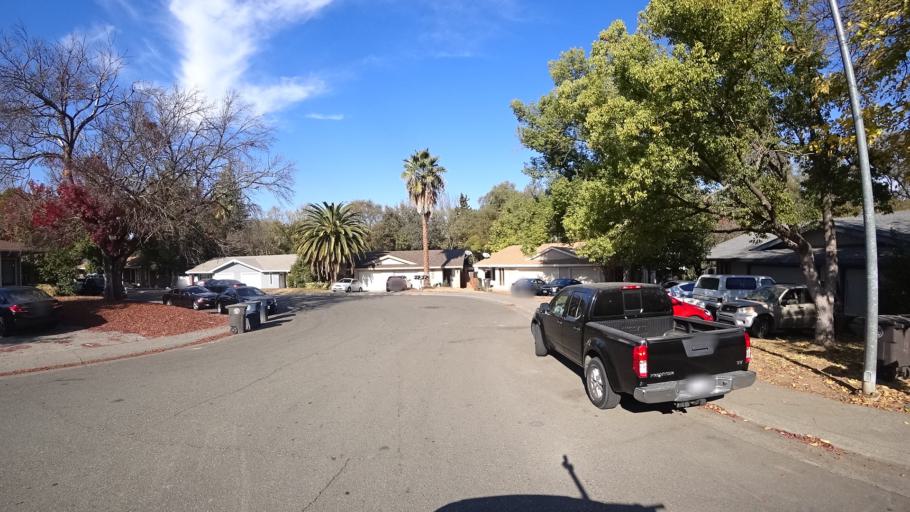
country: US
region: California
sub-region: Sacramento County
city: Fair Oaks
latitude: 38.6674
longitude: -121.2889
